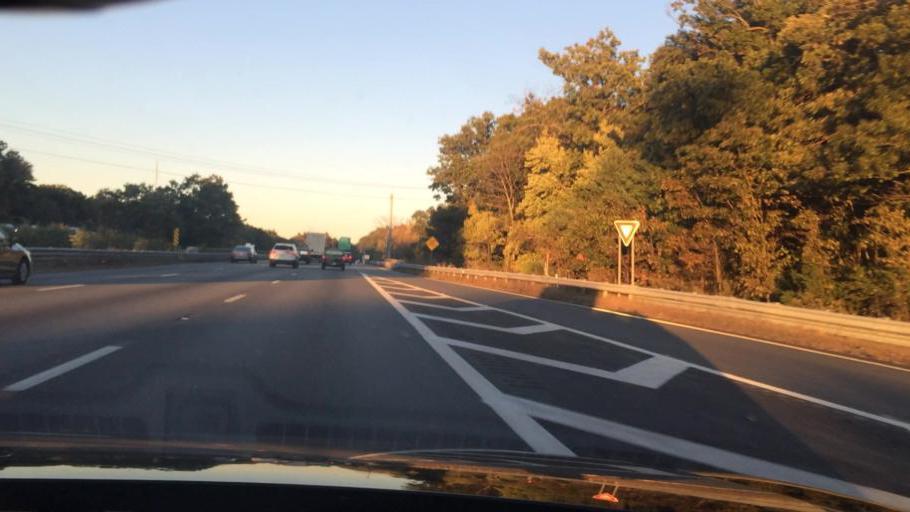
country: US
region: Massachusetts
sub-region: Middlesex County
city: Tewksbury
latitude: 42.6421
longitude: -71.2325
